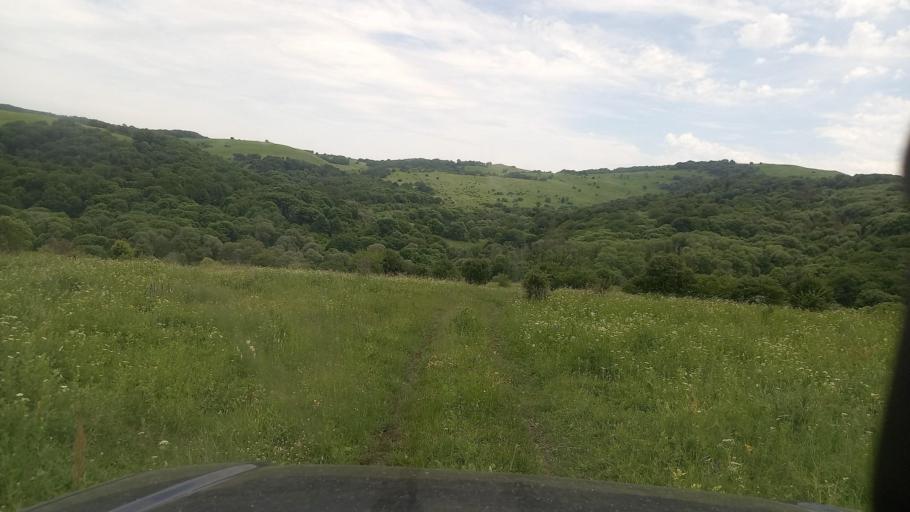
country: RU
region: Karachayevo-Cherkesiya
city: Pregradnaya
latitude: 44.0881
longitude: 41.1942
